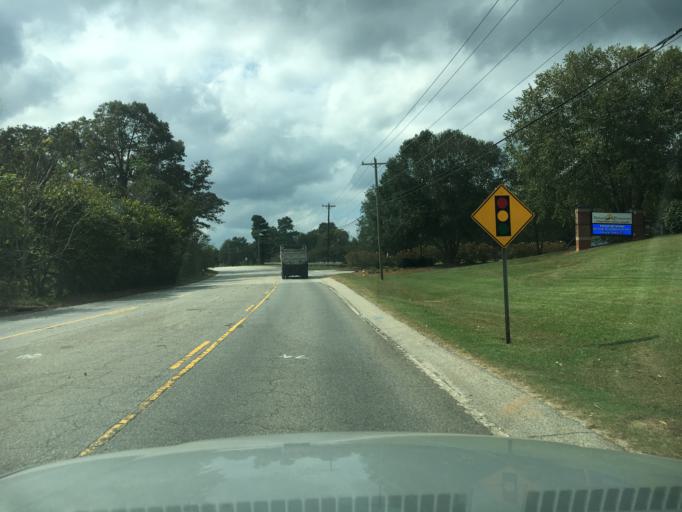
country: US
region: South Carolina
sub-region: Greenville County
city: Tigerville
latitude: 35.0446
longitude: -82.2644
